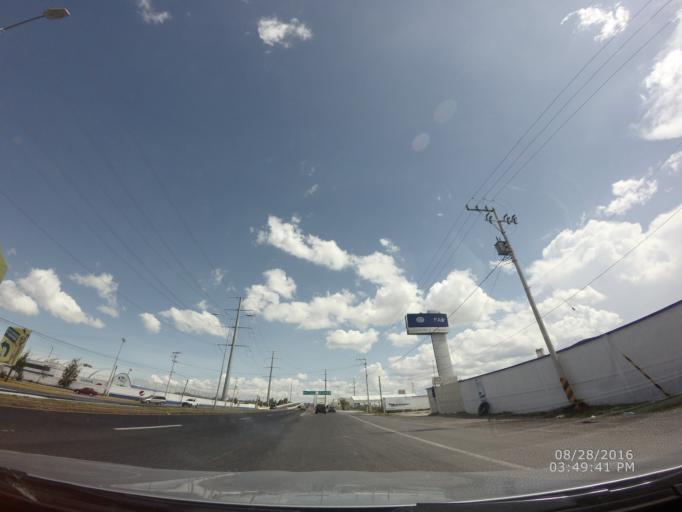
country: MX
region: Hidalgo
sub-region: Mineral de la Reforma
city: Los Tuzos
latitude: 20.0413
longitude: -98.7338
